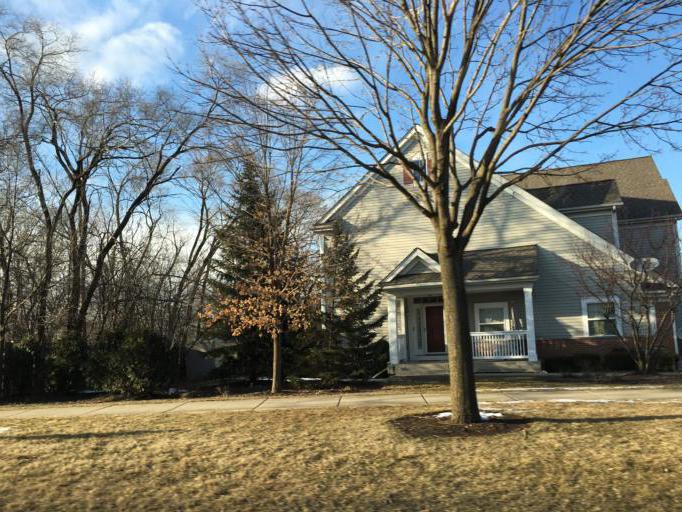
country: US
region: Illinois
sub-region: Cook County
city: Hoffman Estates
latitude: 42.0421
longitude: -88.0832
